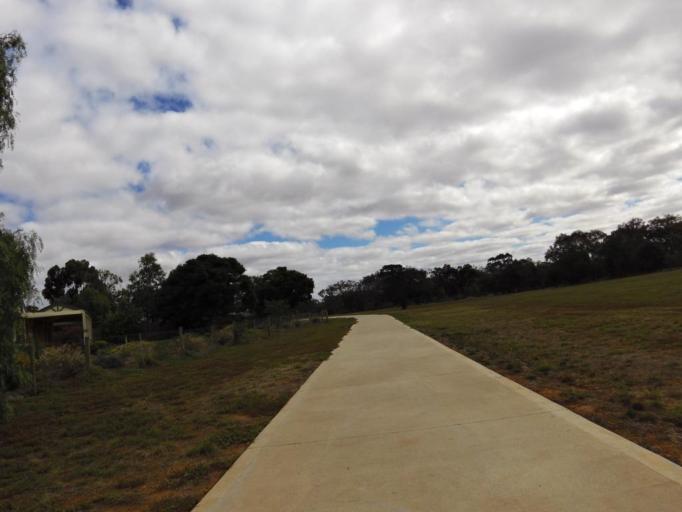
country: AU
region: Victoria
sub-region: Wyndham
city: Tarneit
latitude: -37.8803
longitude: 144.6446
